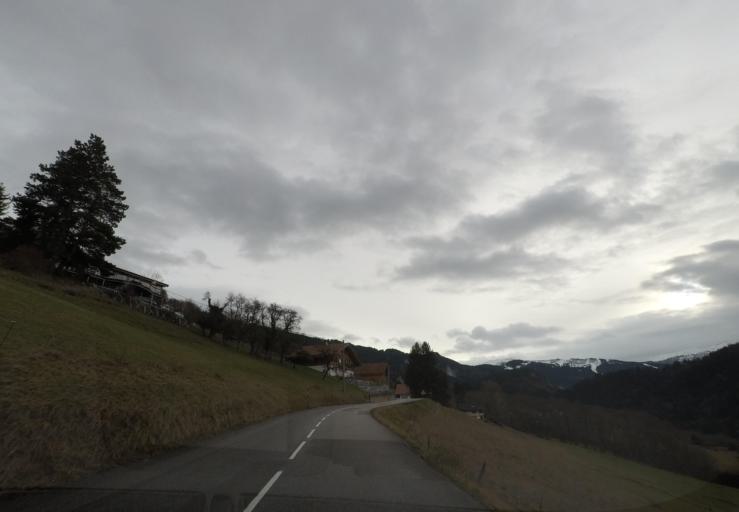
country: FR
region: Rhone-Alpes
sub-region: Departement de la Haute-Savoie
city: Chatillon-sur-Cluses
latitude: 46.0756
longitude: 6.6010
